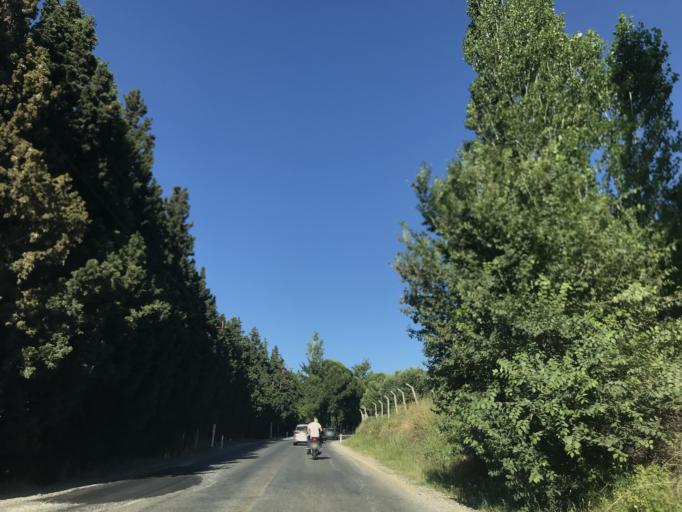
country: TR
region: Aydin
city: Davutlar
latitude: 37.7336
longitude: 27.3228
